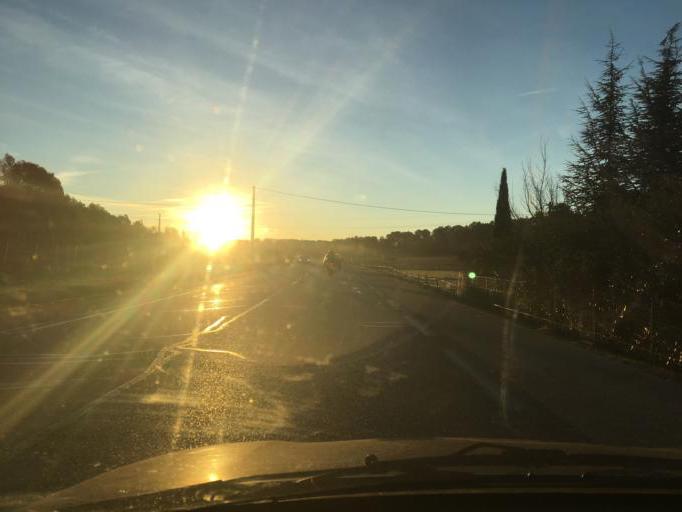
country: FR
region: Provence-Alpes-Cote d'Azur
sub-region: Departement du Var
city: Lorgues
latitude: 43.4707
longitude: 6.3813
